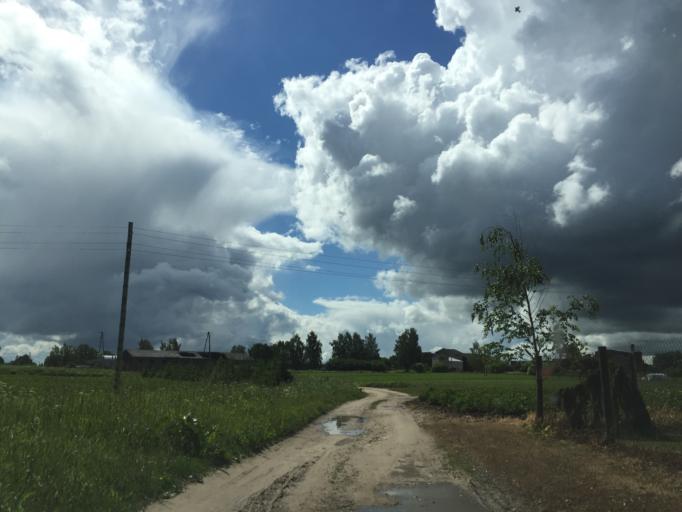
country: LV
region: Lecava
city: Iecava
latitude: 56.6074
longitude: 24.2016
